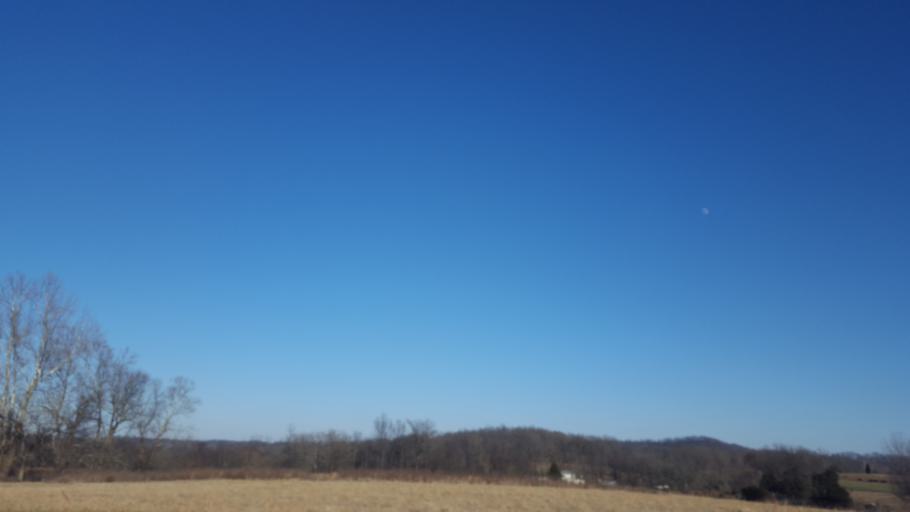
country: US
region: Kentucky
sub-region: Crittenden County
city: Marion
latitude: 37.4340
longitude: -88.0484
